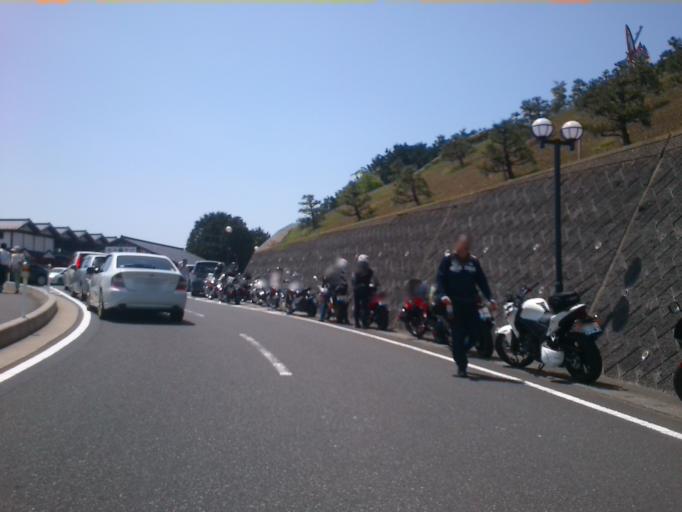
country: JP
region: Kyoto
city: Miyazu
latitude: 35.6751
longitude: 135.2919
